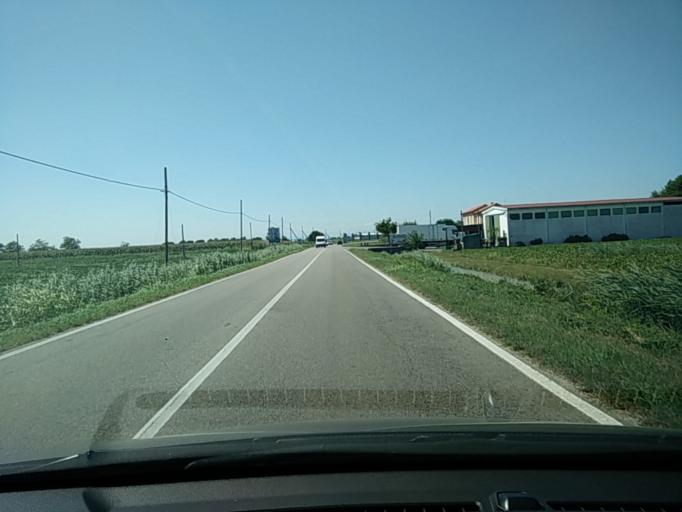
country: IT
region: Veneto
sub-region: Provincia di Venezia
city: Caorle
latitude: 45.6371
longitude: 12.8493
